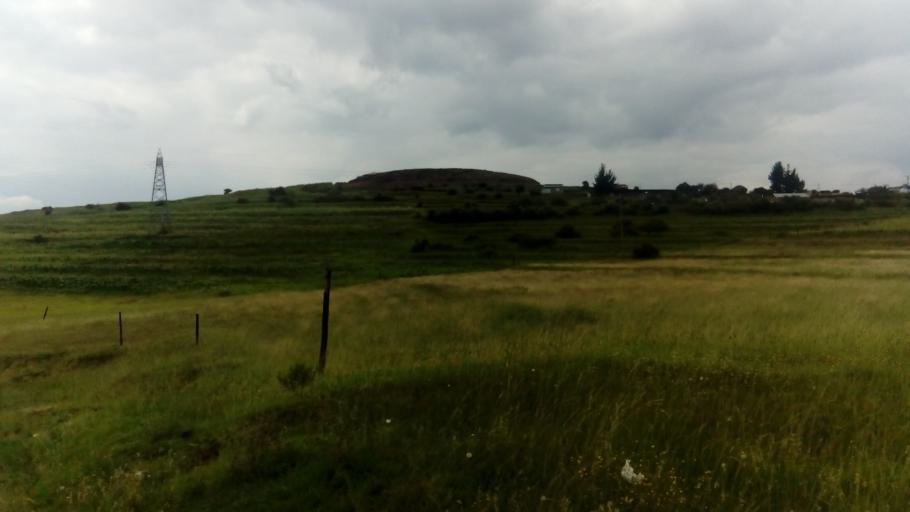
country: LS
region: Leribe
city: Leribe
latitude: -28.9970
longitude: 28.2003
